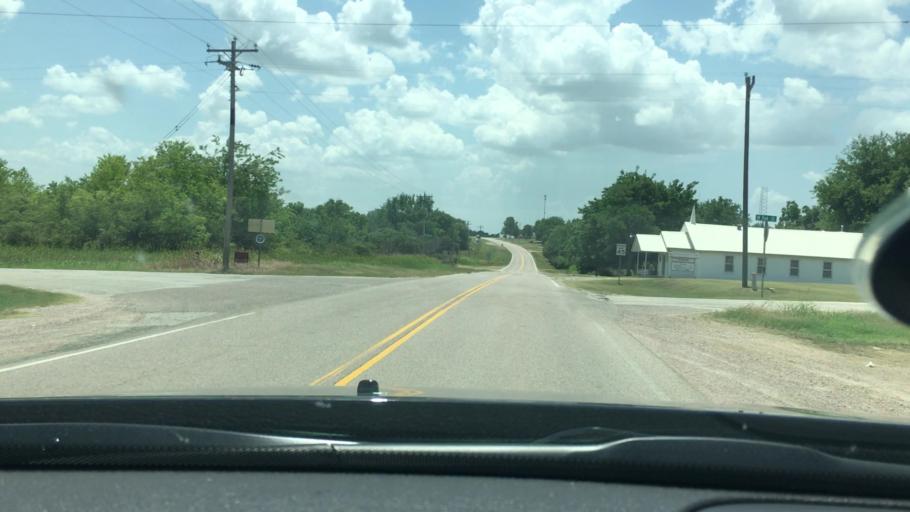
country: US
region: Oklahoma
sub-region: Johnston County
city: Tishomingo
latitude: 34.4488
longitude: -96.6363
